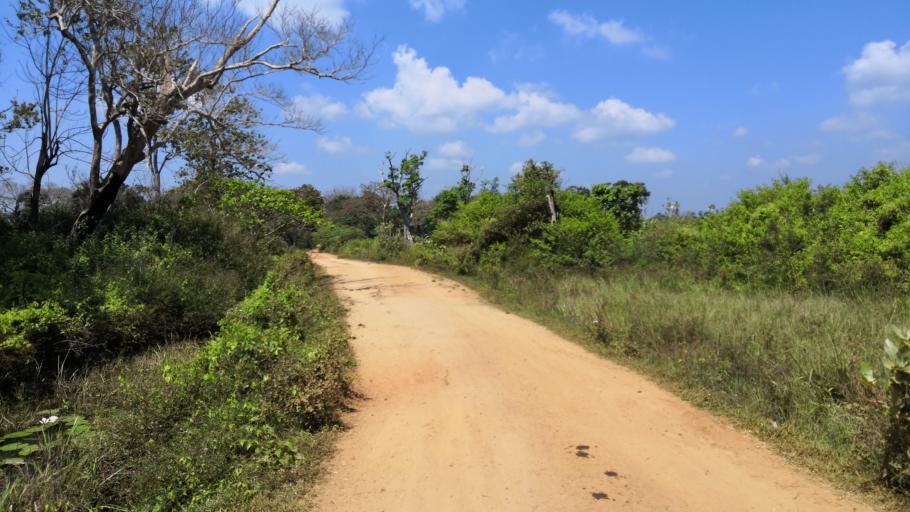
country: LK
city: Padaviya Divisional Secretariat
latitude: 8.9724
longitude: 80.6829
